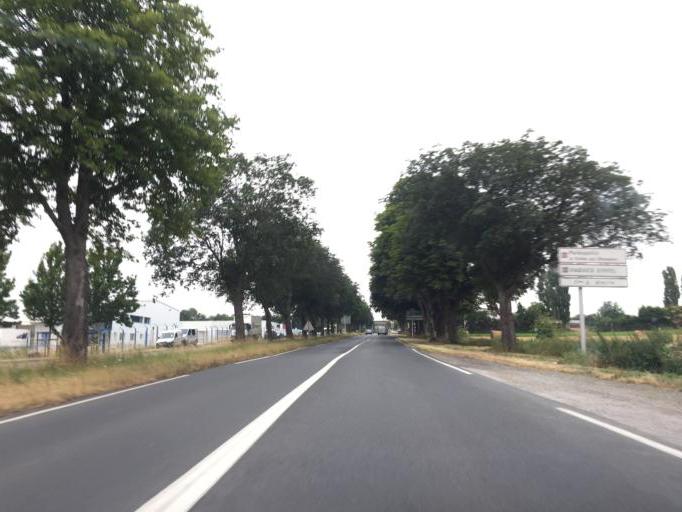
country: FR
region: Auvergne
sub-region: Departement de l'Allier
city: Gannat
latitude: 46.1123
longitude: 3.1998
